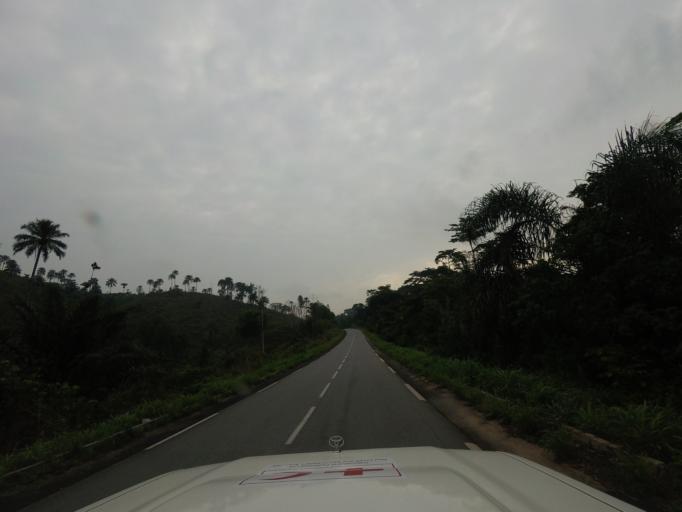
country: LR
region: Lofa
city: Voinjama
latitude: 8.6218
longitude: -9.7441
